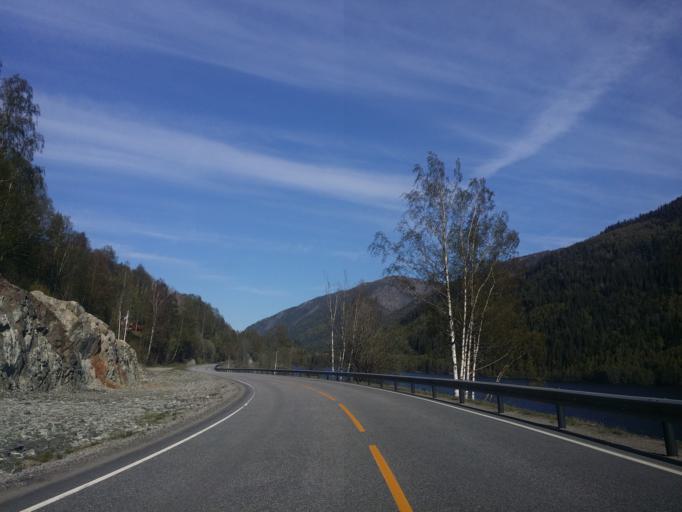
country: NO
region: Telemark
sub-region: Seljord
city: Seljord
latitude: 59.6053
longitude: 8.7235
